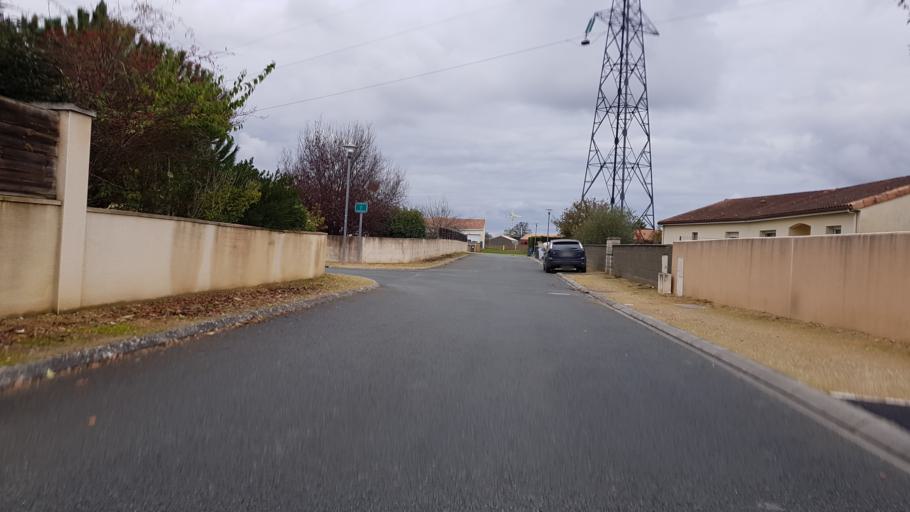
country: FR
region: Poitou-Charentes
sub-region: Departement de la Vienne
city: Chasseneuil-du-Poitou
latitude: 46.6597
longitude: 0.3805
